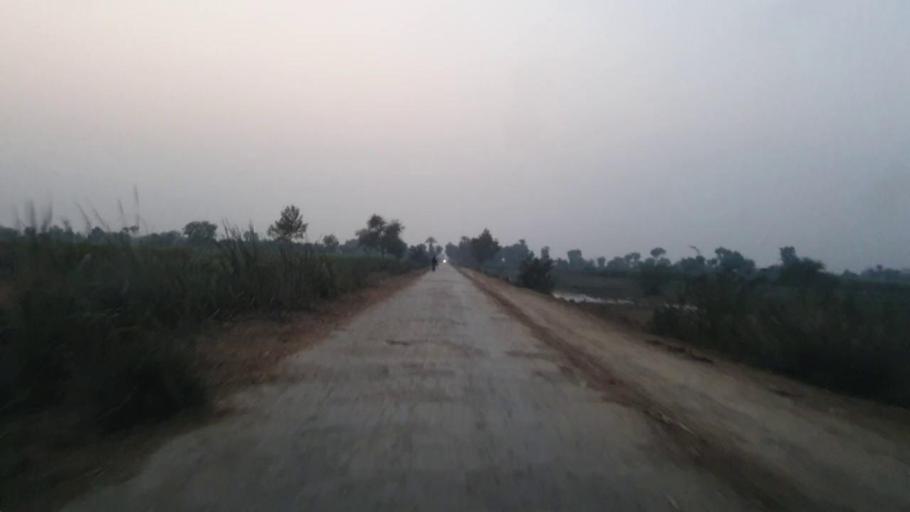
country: PK
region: Sindh
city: Karaundi
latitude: 26.9229
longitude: 68.4259
